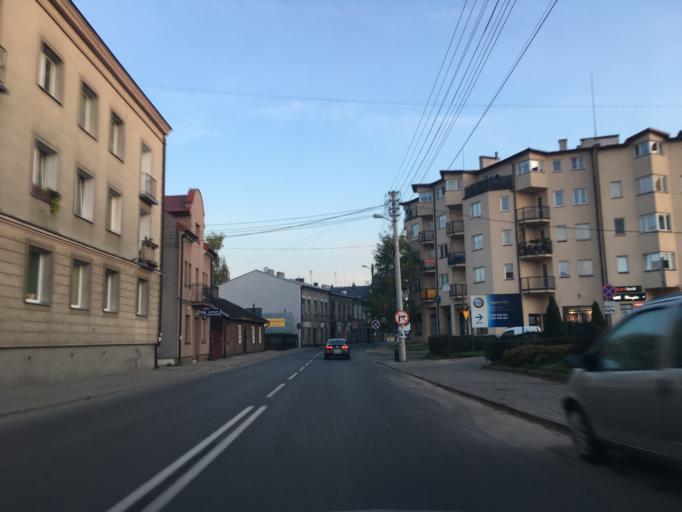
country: PL
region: Lodz Voivodeship
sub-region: Skierniewice
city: Skierniewice
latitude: 51.9577
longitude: 20.1447
